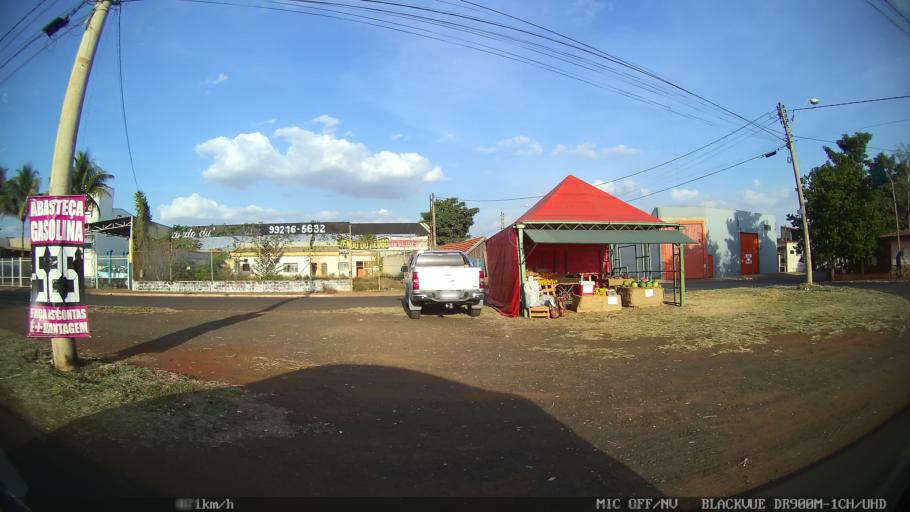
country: BR
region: Sao Paulo
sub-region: Ribeirao Preto
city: Ribeirao Preto
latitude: -21.1285
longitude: -47.7864
